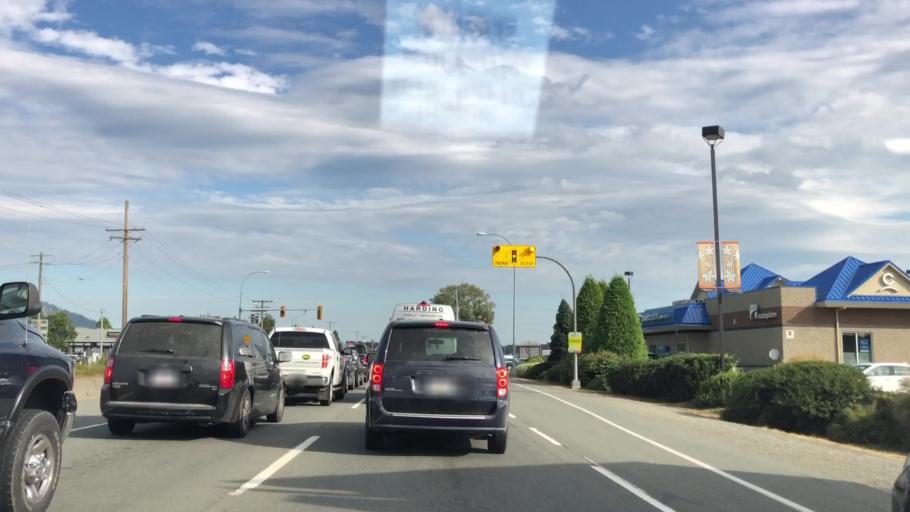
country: CA
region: British Columbia
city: Duncan
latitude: 48.7872
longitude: -123.7074
